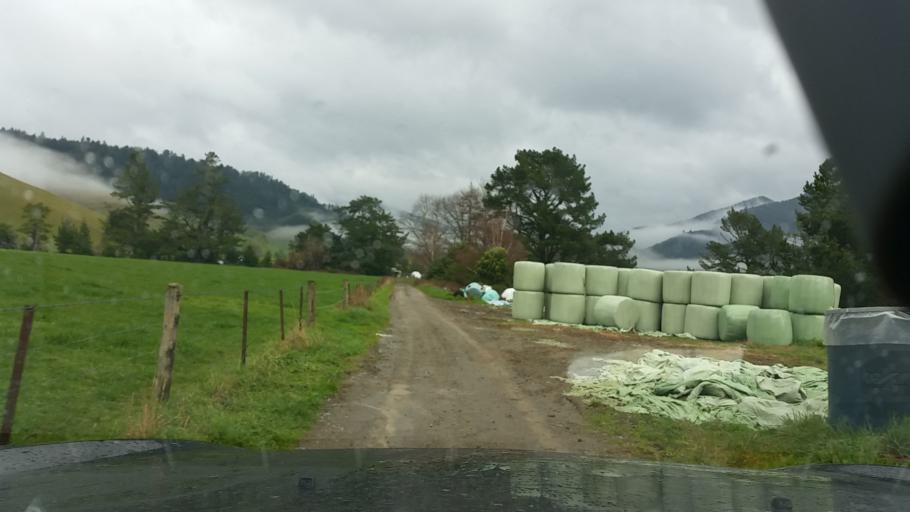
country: NZ
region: Nelson
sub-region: Nelson City
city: Nelson
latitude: -41.2472
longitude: 173.5856
